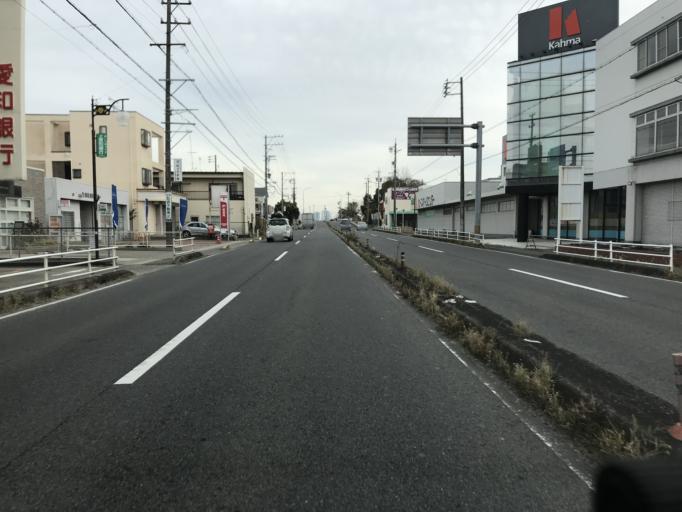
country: JP
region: Aichi
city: Kanie
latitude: 35.1852
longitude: 136.7871
